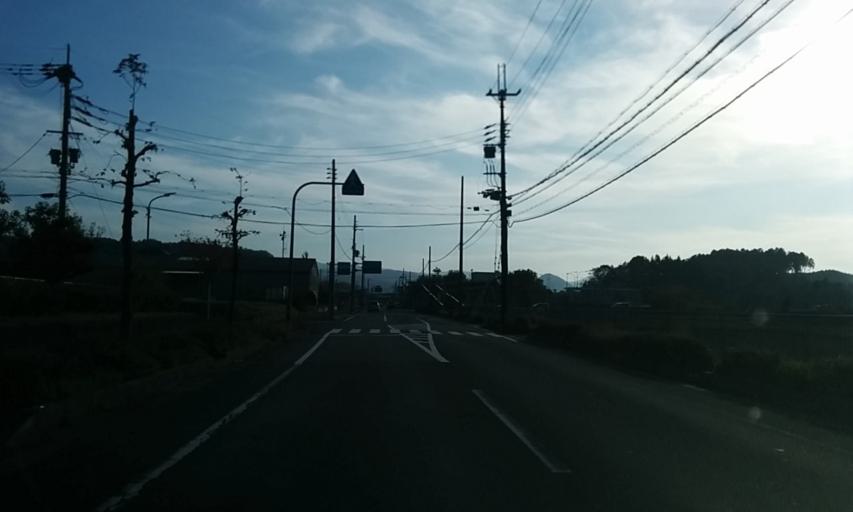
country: JP
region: Kyoto
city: Kameoka
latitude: 35.1263
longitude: 135.4831
